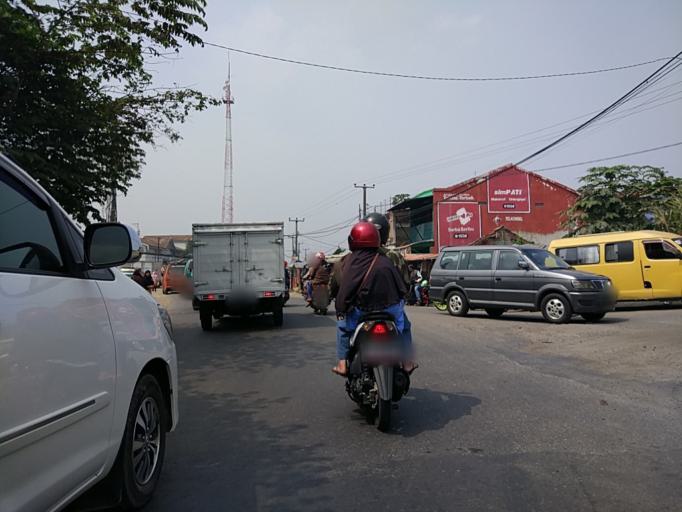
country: ID
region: West Java
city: Padalarang
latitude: -6.8426
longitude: 107.4964
